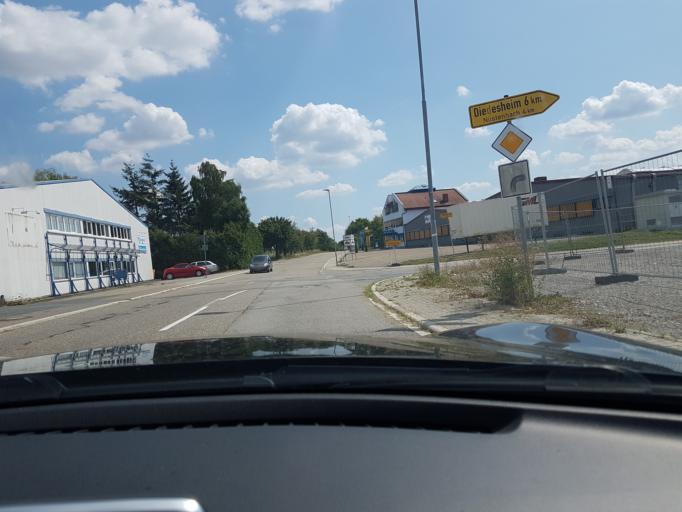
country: DE
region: Baden-Wuerttemberg
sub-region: Karlsruhe Region
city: Fahrenbach
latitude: 49.3962
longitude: 9.1243
